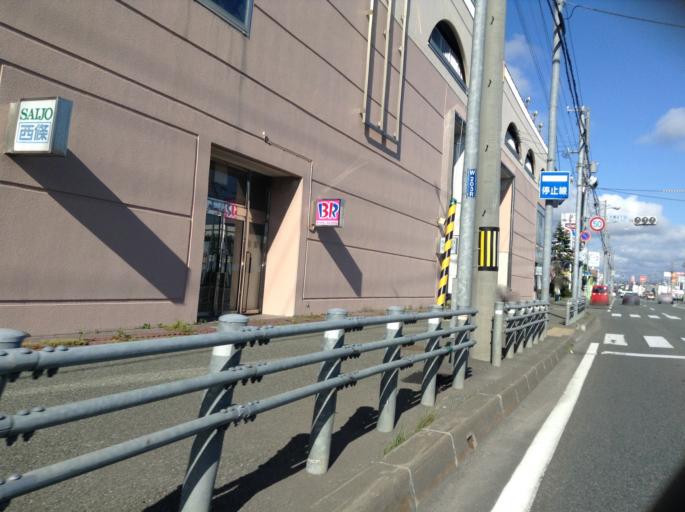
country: JP
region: Hokkaido
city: Wakkanai
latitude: 45.3973
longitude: 141.6919
